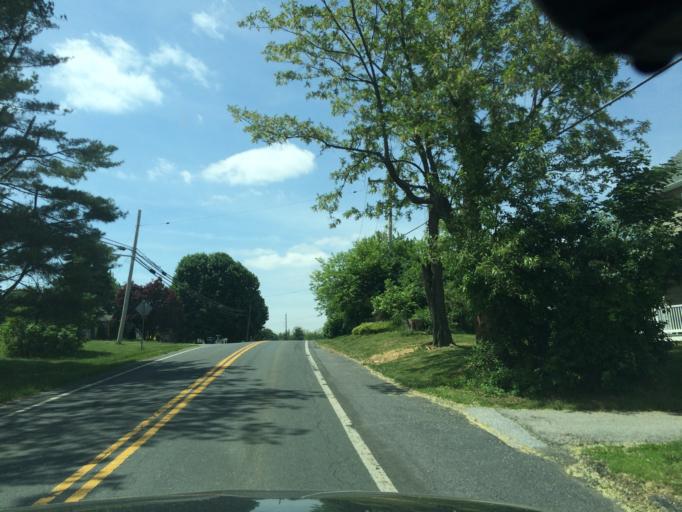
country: US
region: Maryland
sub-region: Carroll County
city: Westminster
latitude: 39.5490
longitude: -76.9508
